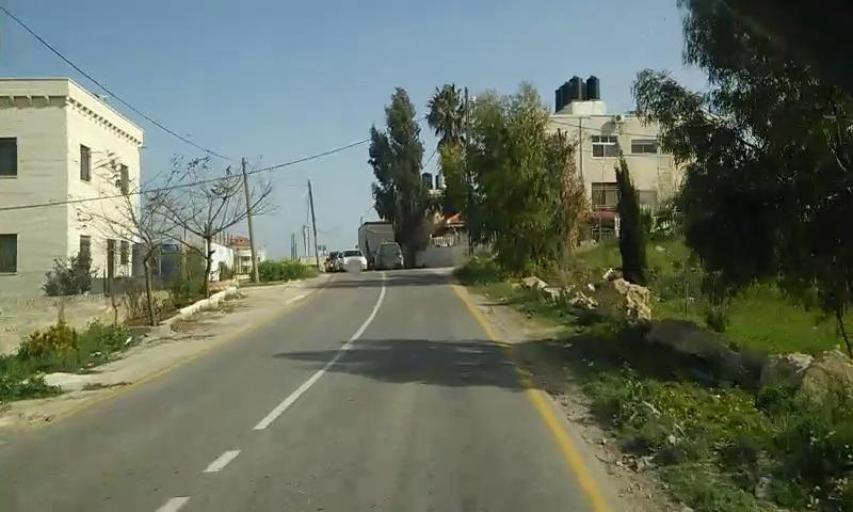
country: PS
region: West Bank
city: Surda
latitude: 31.9413
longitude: 35.2137
